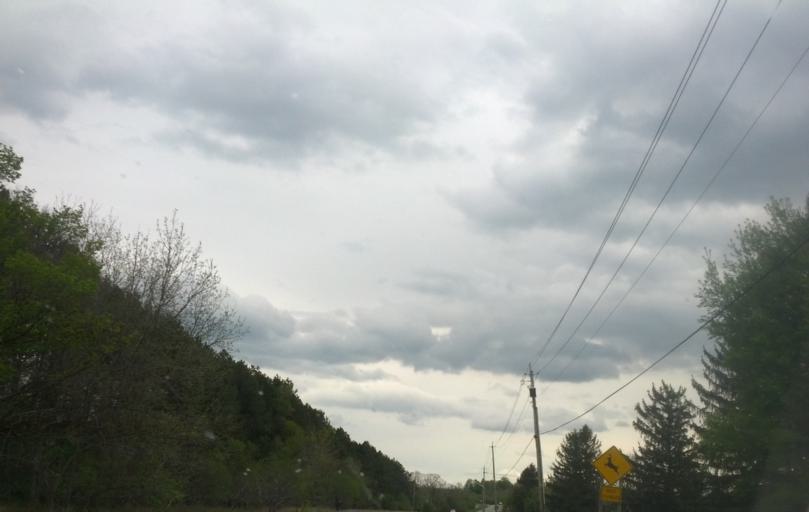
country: US
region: New York
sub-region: Onondaga County
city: Fayetteville
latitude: 42.9922
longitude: -76.0480
